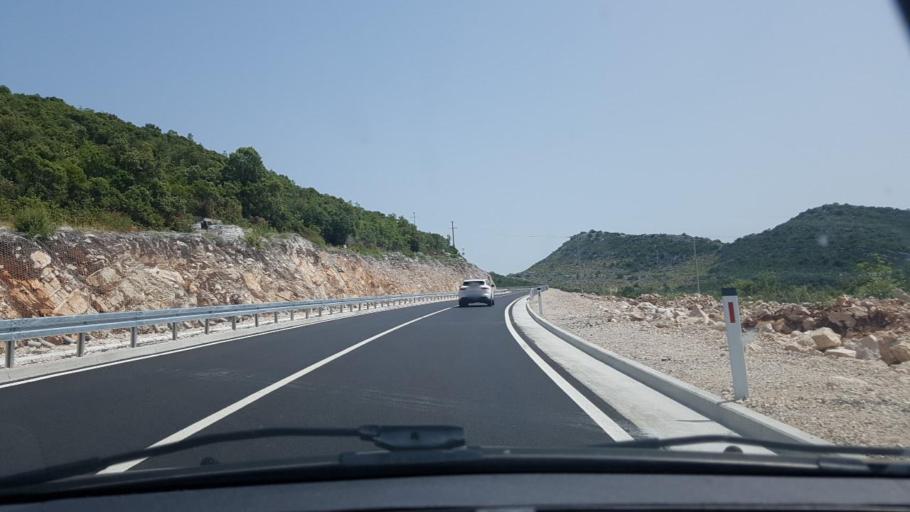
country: HR
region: Dubrovacko-Neretvanska
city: Ston
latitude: 42.9508
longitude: 17.7583
